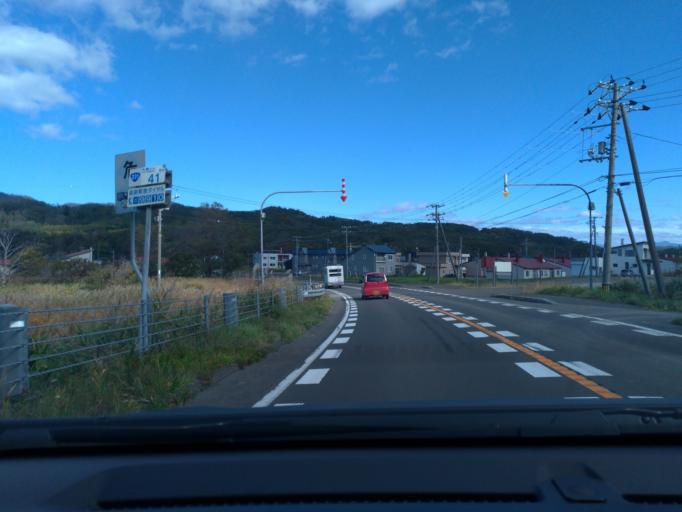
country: JP
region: Hokkaido
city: Ishikari
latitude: 43.3952
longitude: 141.4365
